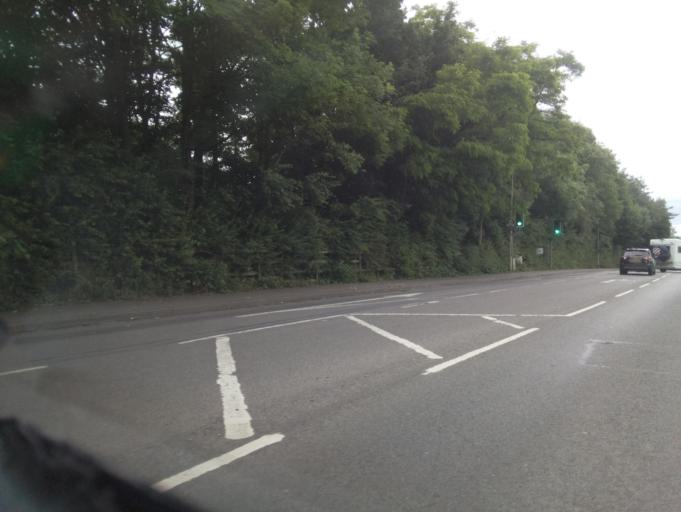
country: GB
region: England
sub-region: Leicestershire
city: Coalville
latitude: 52.7292
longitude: -1.3669
